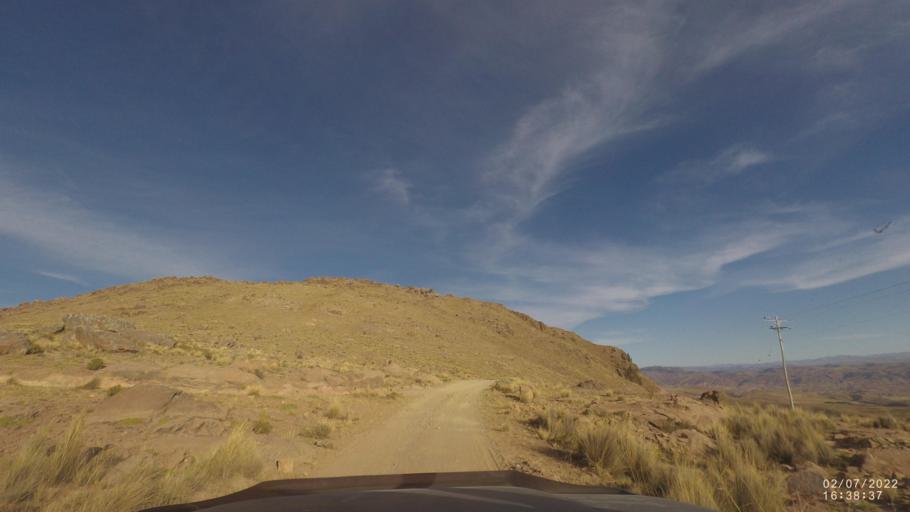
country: BO
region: Cochabamba
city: Irpa Irpa
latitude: -17.9710
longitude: -66.4956
